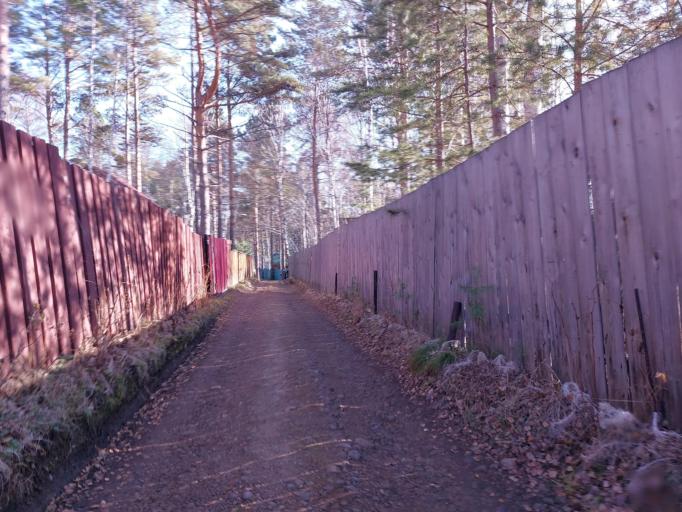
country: RU
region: Irkutsk
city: Pivovarikha
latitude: 52.1873
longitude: 104.4630
